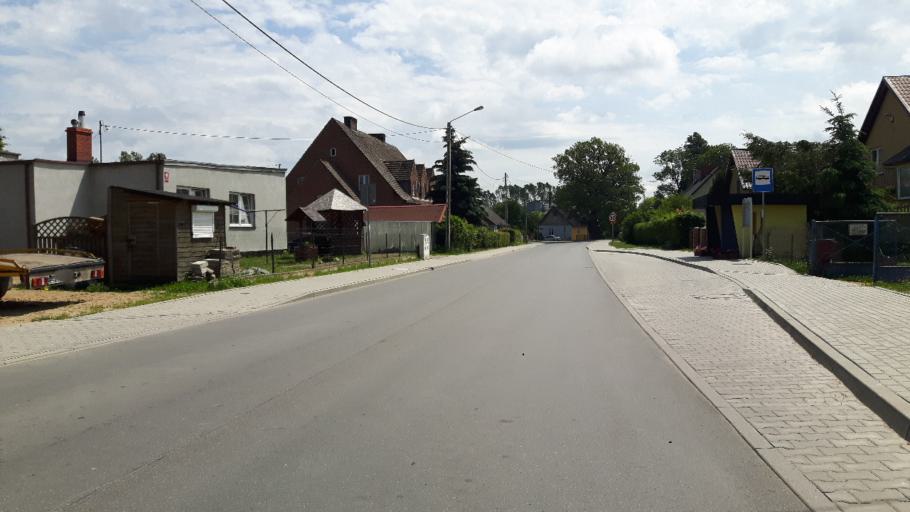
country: PL
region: Pomeranian Voivodeship
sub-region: Powiat wejherowski
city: Choczewo
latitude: 54.7371
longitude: 17.8281
